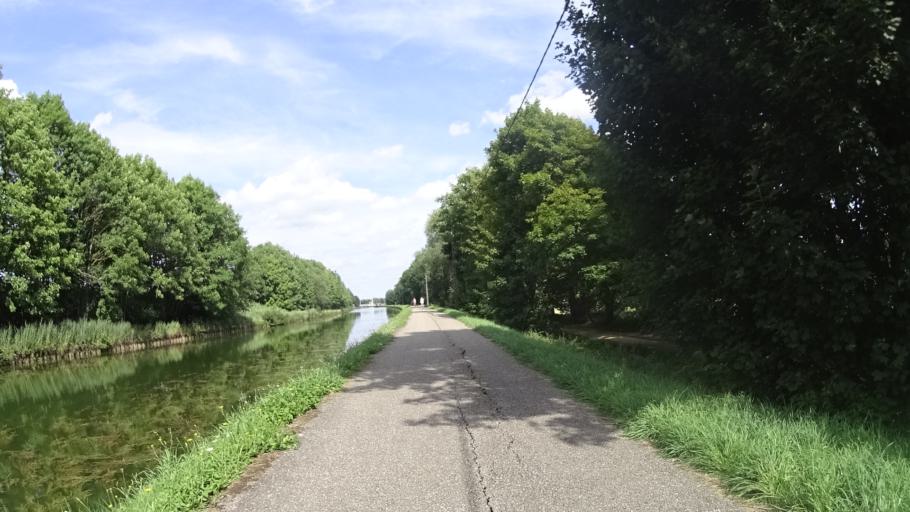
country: FR
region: Lorraine
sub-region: Departement de Meurthe-et-Moselle
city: Toul
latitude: 48.6771
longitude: 5.8750
